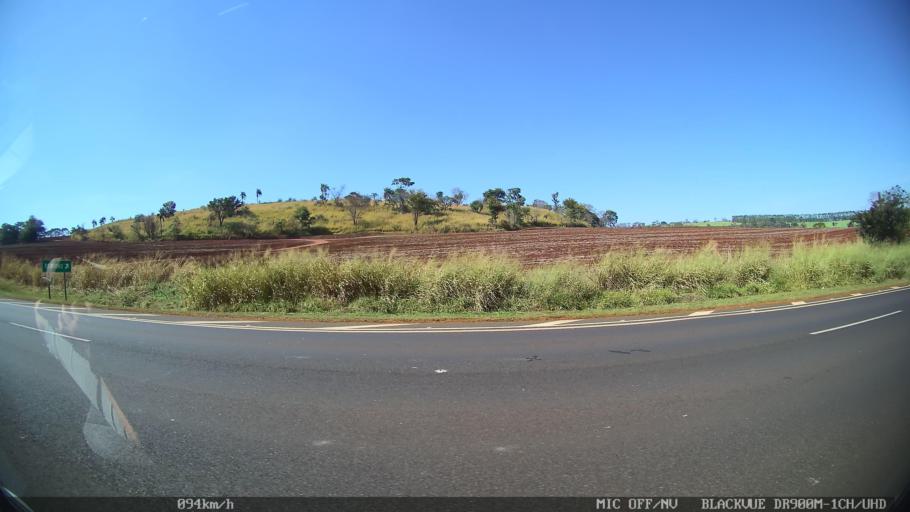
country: BR
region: Sao Paulo
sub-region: Franca
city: Franca
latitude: -20.6133
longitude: -47.4558
